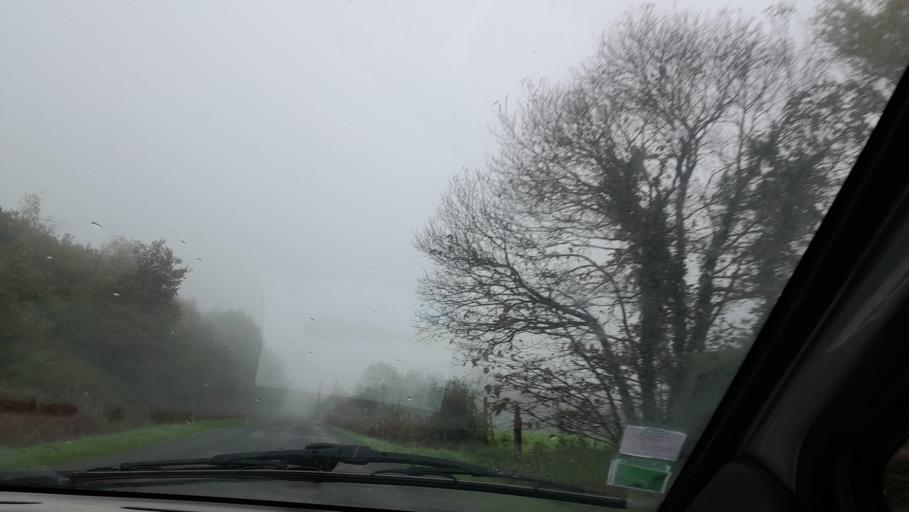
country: FR
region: Pays de la Loire
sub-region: Departement de la Mayenne
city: Saint-Pierre-la-Cour
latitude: 48.0946
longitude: -1.0168
